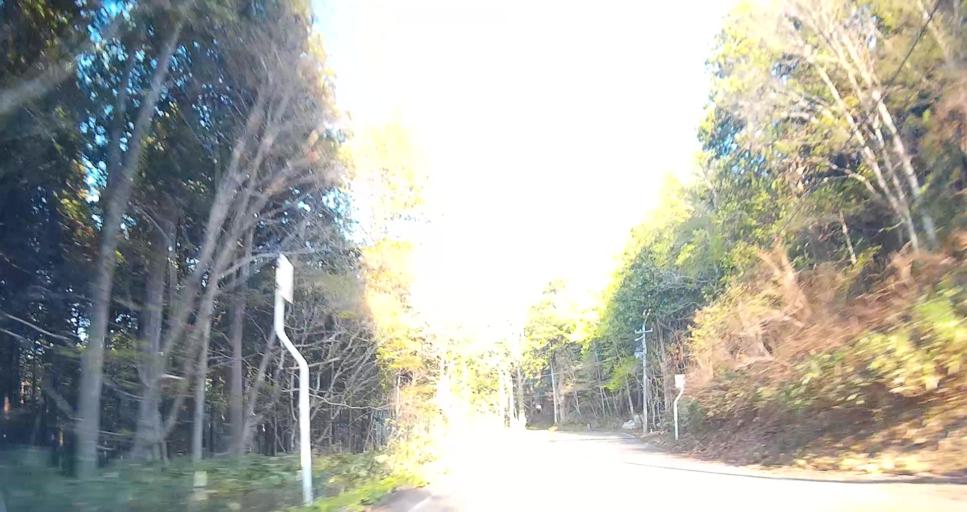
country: JP
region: Aomori
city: Mutsu
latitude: 41.3149
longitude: 141.1250
